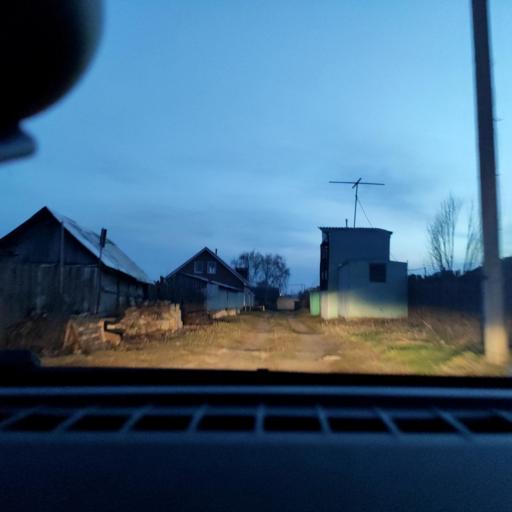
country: RU
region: Samara
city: Zhigulevsk
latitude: 53.5521
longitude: 49.5343
